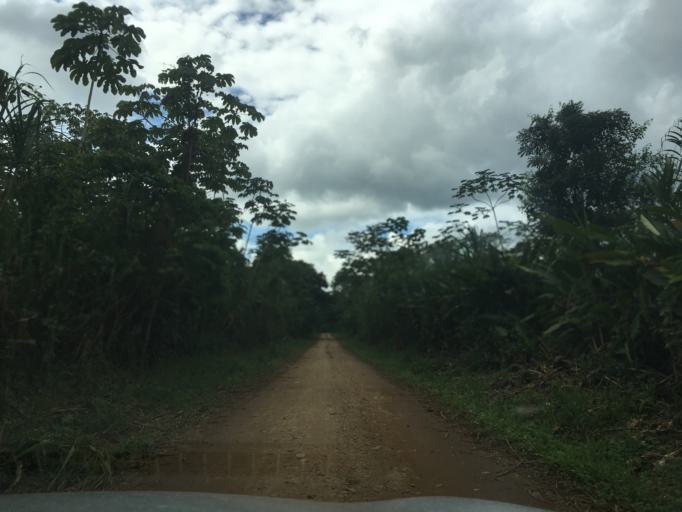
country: BZ
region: Stann Creek
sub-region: Dangriga
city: Dangriga
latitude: 16.9374
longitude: -88.3719
